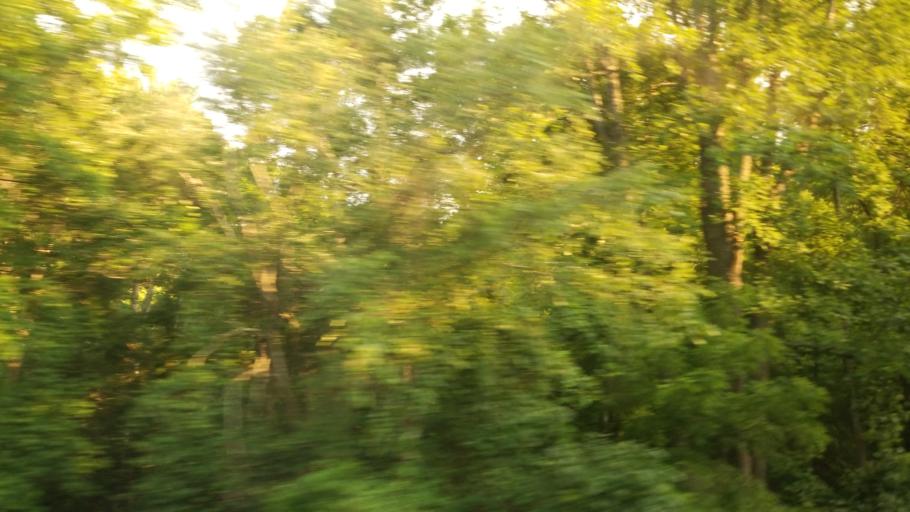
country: US
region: Virginia
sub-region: Fairfax County
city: Fairfax Station
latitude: 38.7925
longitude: -77.3584
